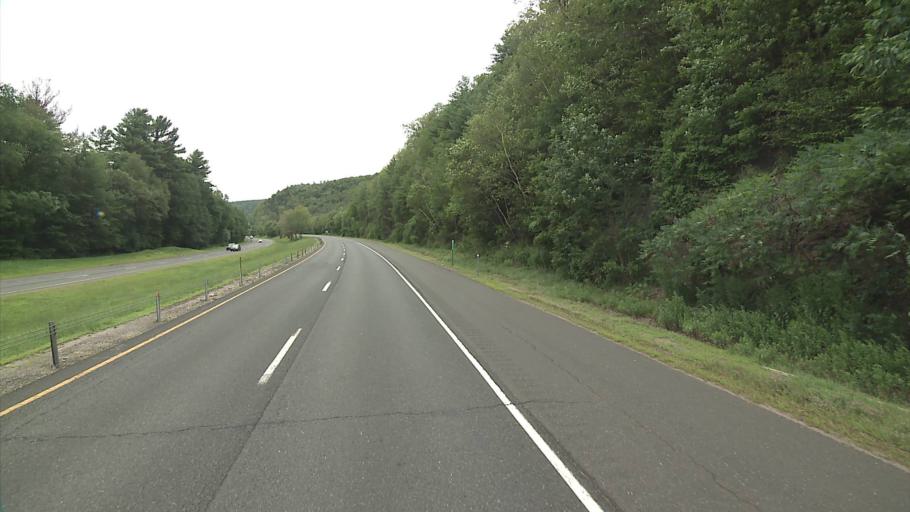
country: US
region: Connecticut
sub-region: Litchfield County
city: Thomaston
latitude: 41.6446
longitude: -73.0825
